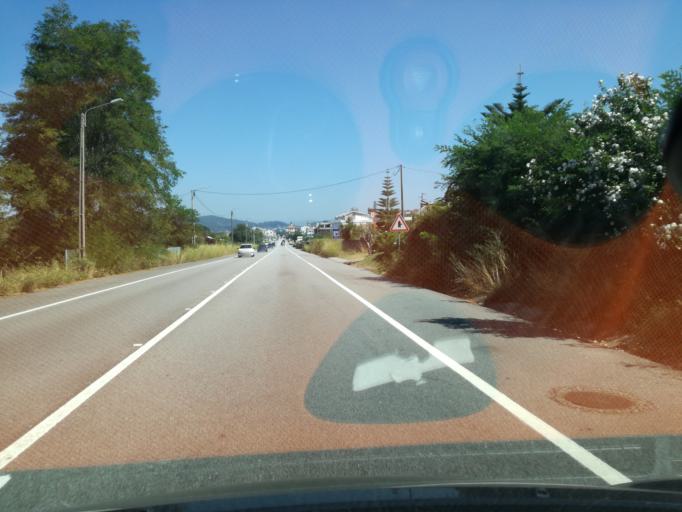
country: ES
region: Galicia
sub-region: Provincia de Pontevedra
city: O Rosal
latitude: 41.8898
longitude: -8.8226
